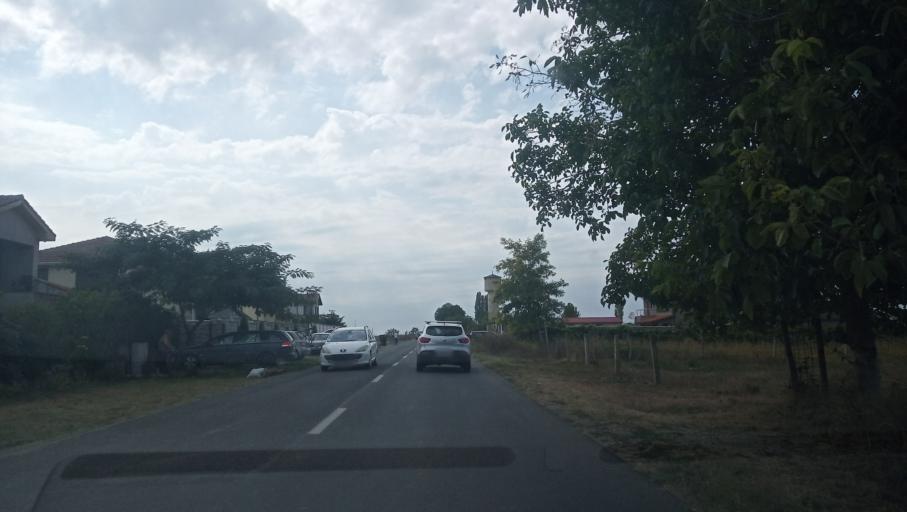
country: RO
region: Constanta
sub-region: Municipiul Mangalia
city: Mangalia
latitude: 43.8162
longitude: 28.5593
